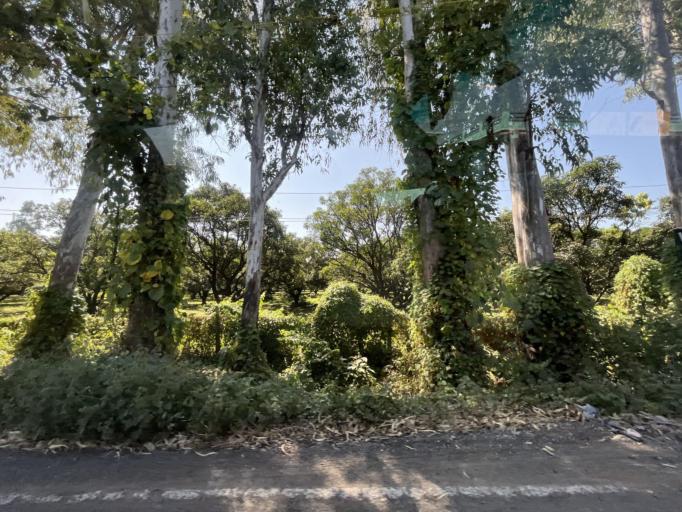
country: IN
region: Uttarakhand
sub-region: Naini Tal
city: Haldwani
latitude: 29.2131
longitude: 79.4564
